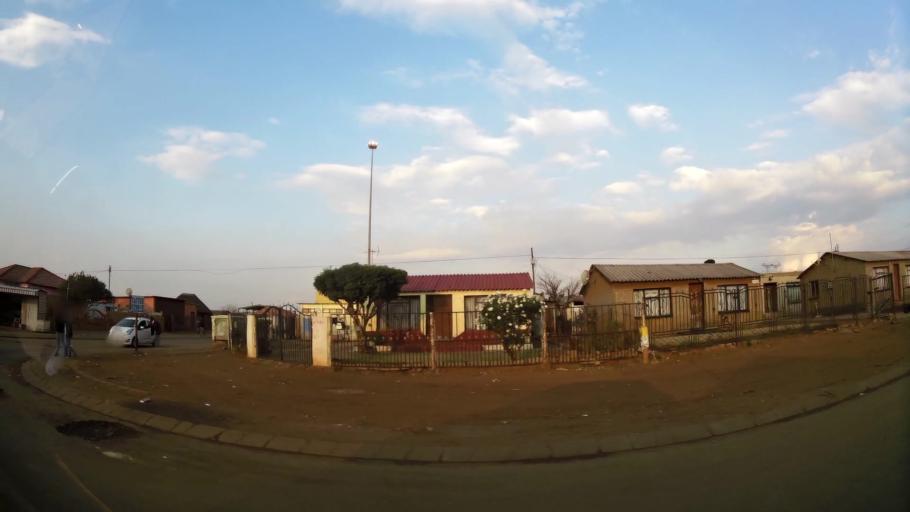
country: ZA
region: Gauteng
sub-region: City of Johannesburg Metropolitan Municipality
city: Orange Farm
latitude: -26.5573
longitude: 27.8621
